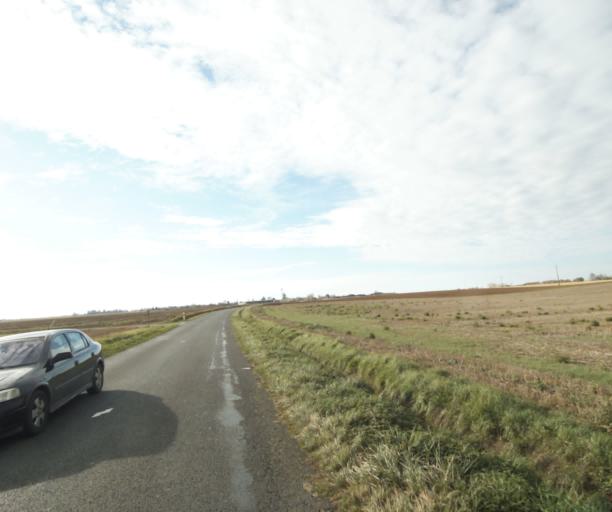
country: FR
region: Poitou-Charentes
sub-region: Departement de la Charente-Maritime
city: Corme-Royal
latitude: 45.7290
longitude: -0.8196
